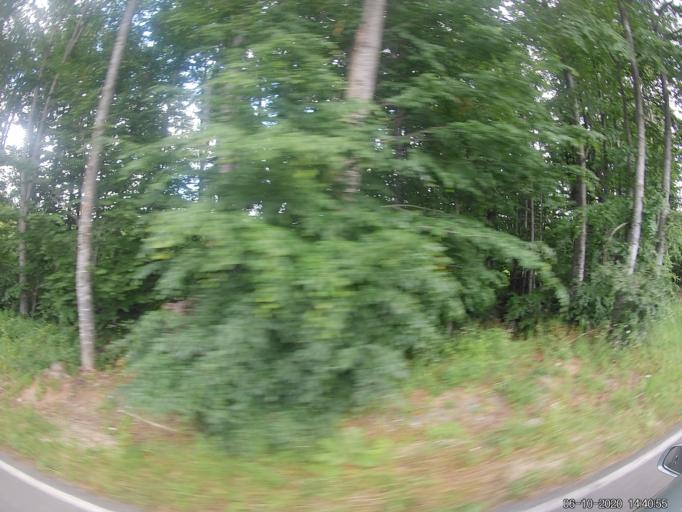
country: XK
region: Prizren
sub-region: Komuna e Therandes
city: Budakovo
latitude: 42.3931
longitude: 20.9438
